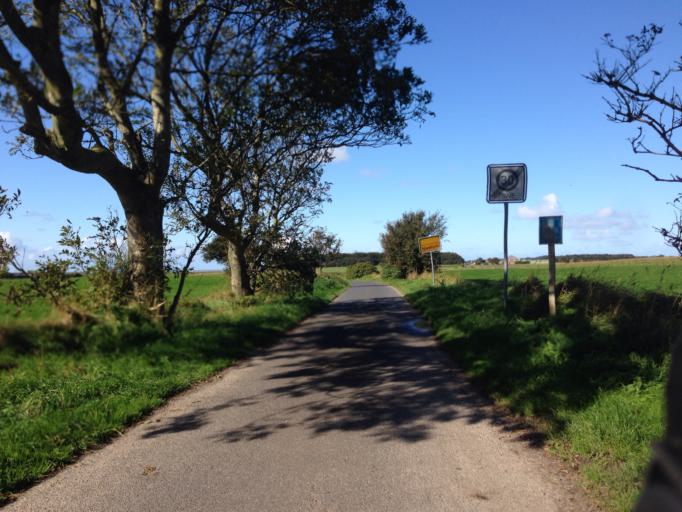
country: DE
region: Schleswig-Holstein
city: Borgsum
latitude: 54.6890
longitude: 8.4691
